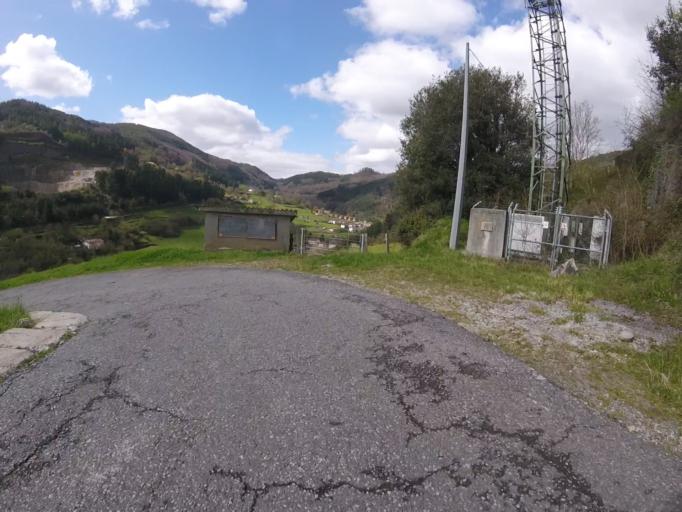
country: ES
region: Basque Country
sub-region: Provincia de Guipuzcoa
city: Albiztur
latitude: 43.1306
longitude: -2.1264
